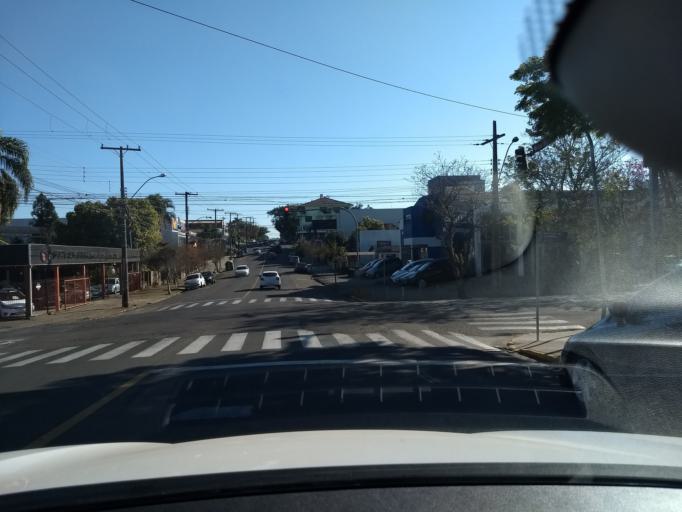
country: BR
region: Rio Grande do Sul
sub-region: Santa Cruz Do Sul
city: Santa Cruz do Sul
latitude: -29.7174
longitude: -52.4415
